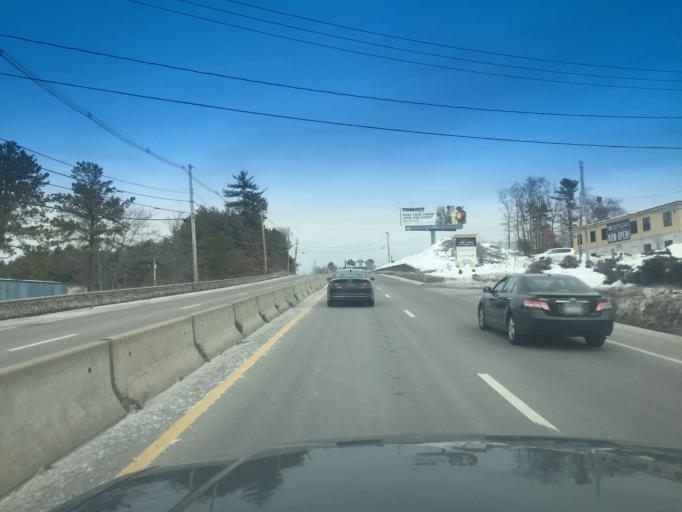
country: US
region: Massachusetts
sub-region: Norfolk County
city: Walpole
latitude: 42.1178
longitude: -71.2360
